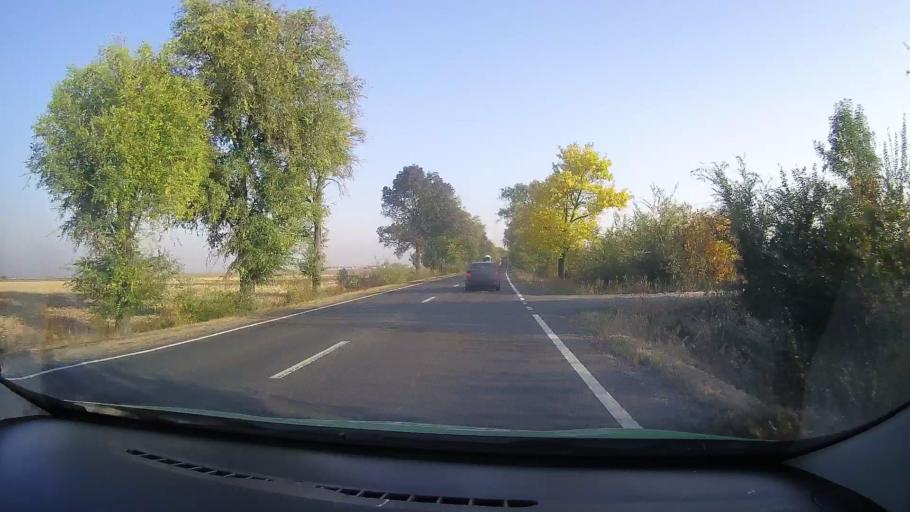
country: RO
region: Arad
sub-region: Comuna Simand
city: Simand
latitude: 46.3679
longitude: 21.4282
